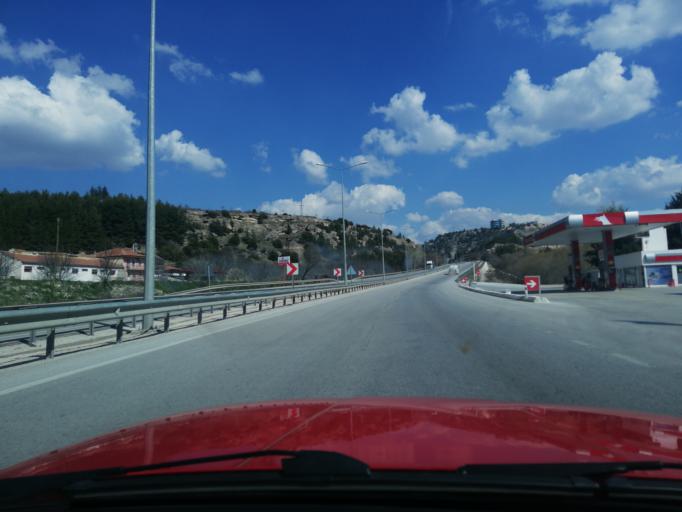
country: TR
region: Burdur
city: Burdur
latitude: 37.6987
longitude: 30.3248
